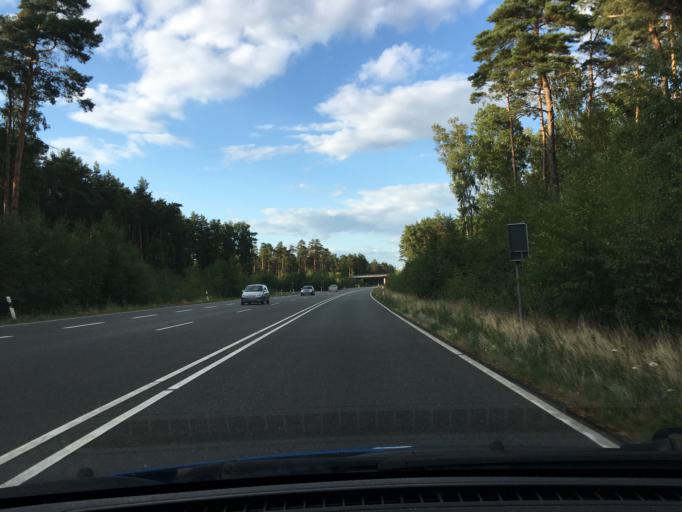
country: DE
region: Lower Saxony
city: Adelheidsdorf
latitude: 52.5573
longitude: 10.0695
